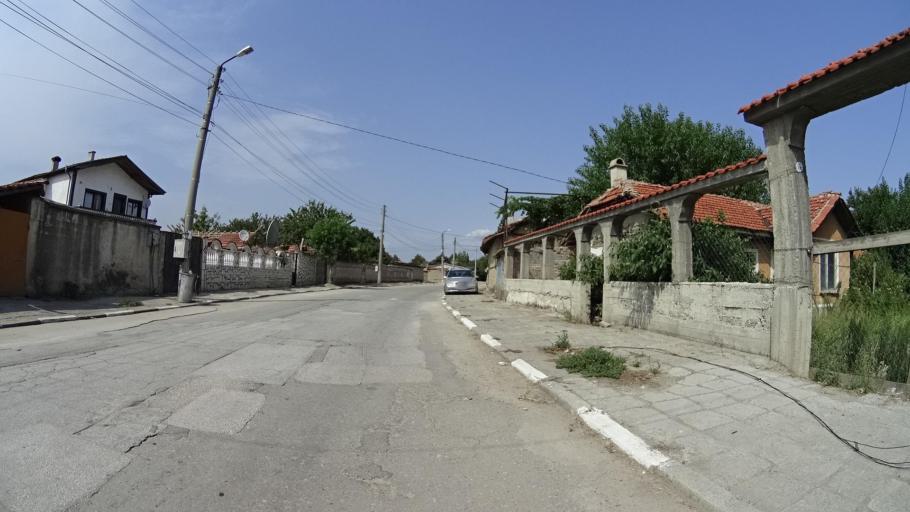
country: BG
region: Plovdiv
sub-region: Obshtina Kaloyanovo
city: Kaloyanovo
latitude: 42.2665
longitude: 24.7998
